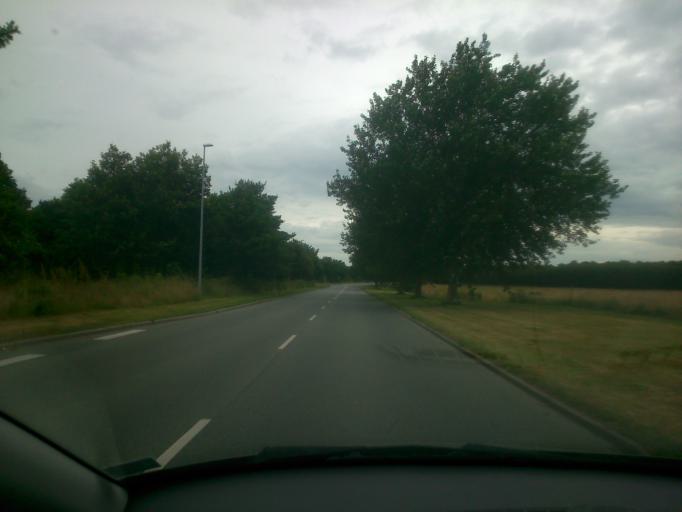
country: DK
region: South Denmark
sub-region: Esbjerg Kommune
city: Esbjerg
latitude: 55.5175
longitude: 8.4250
